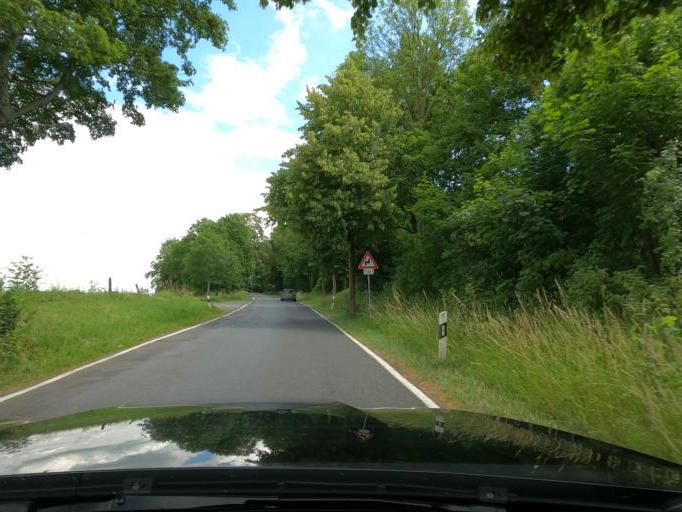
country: DE
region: Lower Saxony
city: Elbe
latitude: 52.1222
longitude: 10.2951
